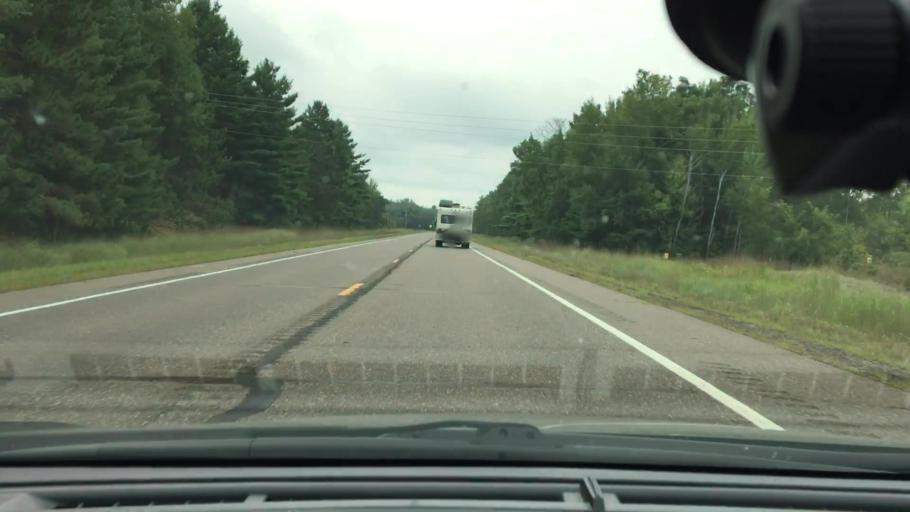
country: US
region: Minnesota
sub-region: Crow Wing County
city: Crosby
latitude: 46.4973
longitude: -93.9572
